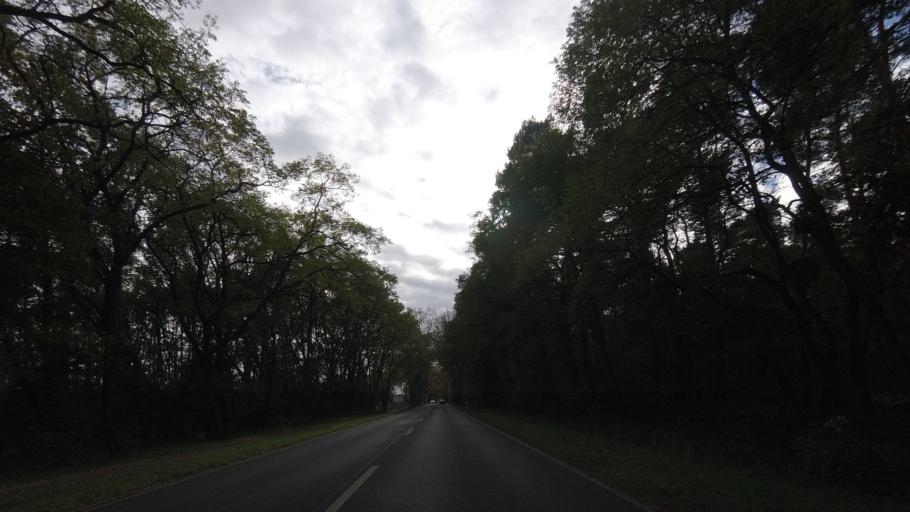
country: DE
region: Brandenburg
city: Beelitz
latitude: 52.2009
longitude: 12.9566
